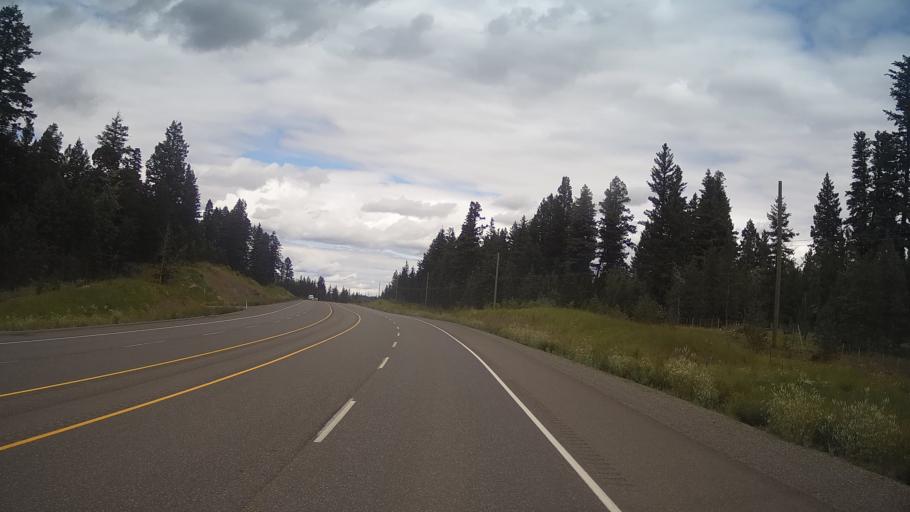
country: CA
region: British Columbia
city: Cache Creek
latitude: 51.4089
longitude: -121.3751
